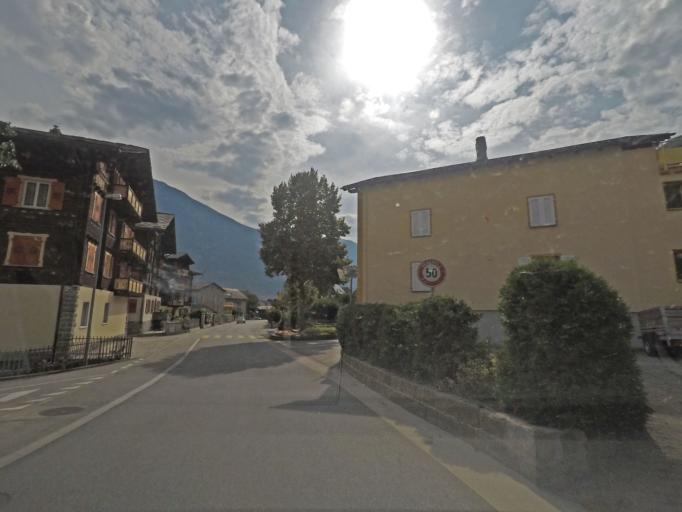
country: CH
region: Valais
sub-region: Brig District
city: Naters
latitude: 46.3269
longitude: 7.9899
